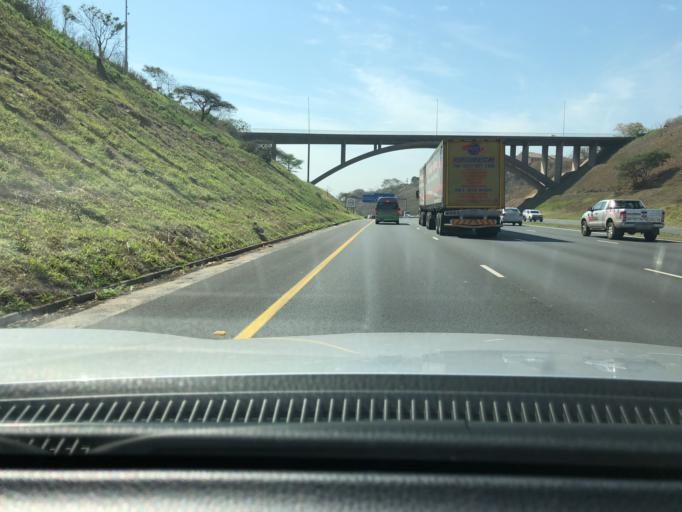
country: ZA
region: KwaZulu-Natal
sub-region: eThekwini Metropolitan Municipality
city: Berea
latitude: -29.8187
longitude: 30.9700
